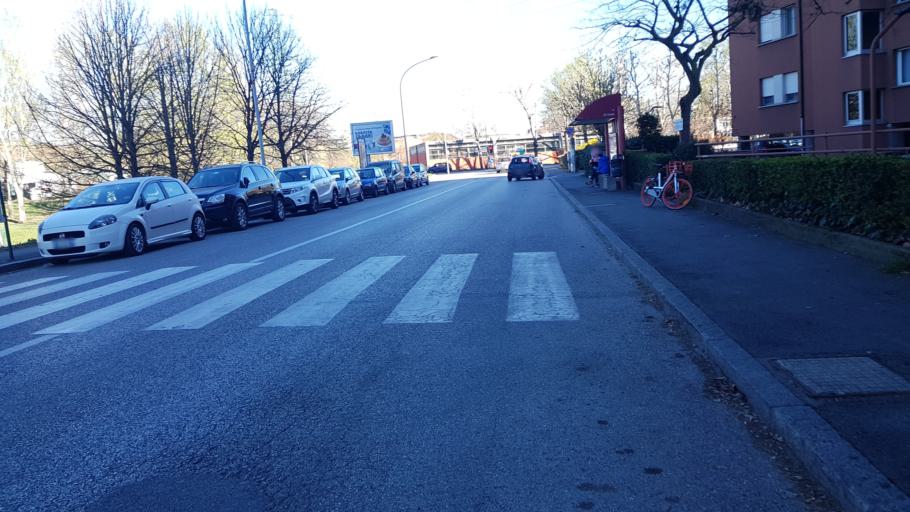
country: IT
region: Emilia-Romagna
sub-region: Provincia di Bologna
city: Bologna
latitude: 44.5218
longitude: 11.3280
